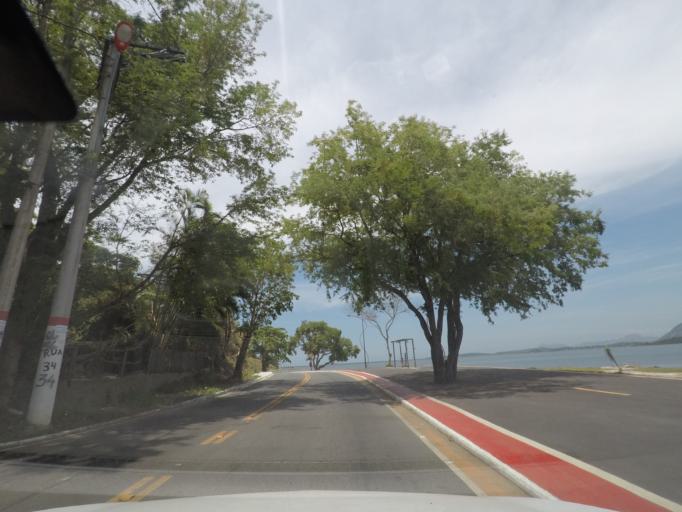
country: BR
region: Rio de Janeiro
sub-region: Marica
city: Marica
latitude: -22.9312
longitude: -42.8275
